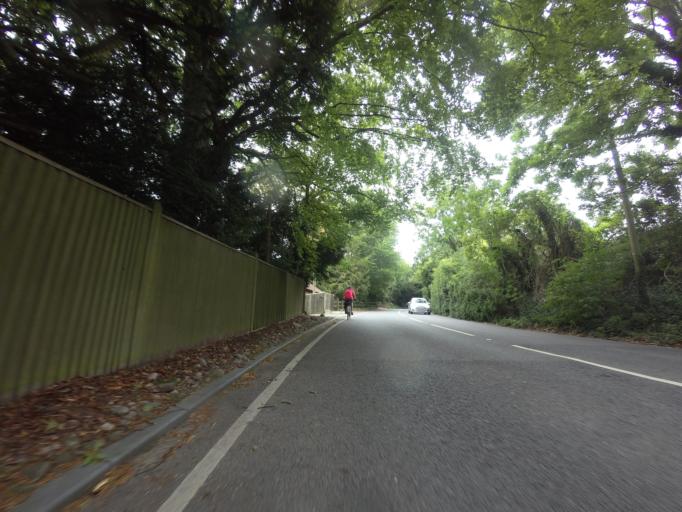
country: GB
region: England
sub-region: Kent
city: Shoreham
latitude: 51.3207
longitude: 0.1911
